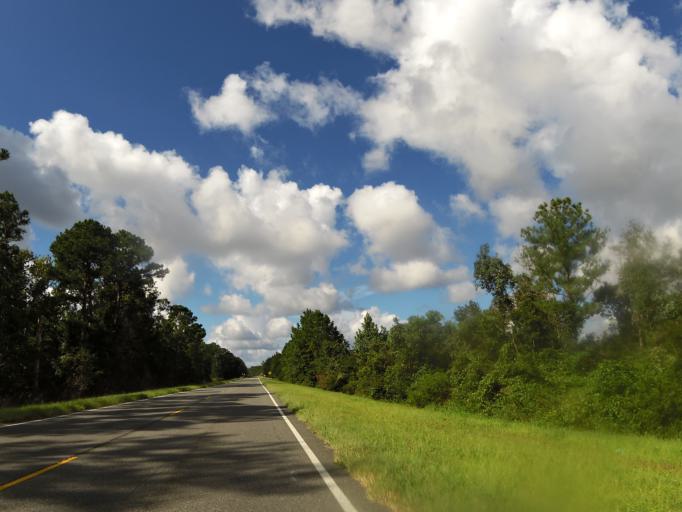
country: US
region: Georgia
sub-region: Camden County
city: Kingsland
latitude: 30.7712
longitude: -81.6869
